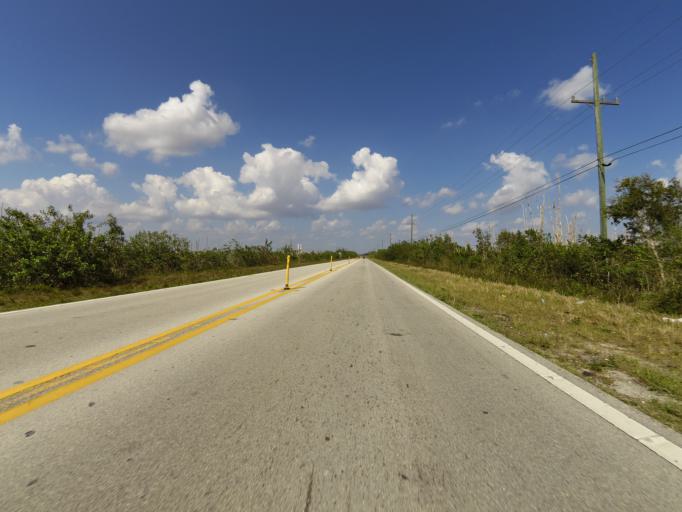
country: US
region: Florida
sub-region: Miami-Dade County
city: Palm Springs North
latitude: 25.9345
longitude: -80.4459
